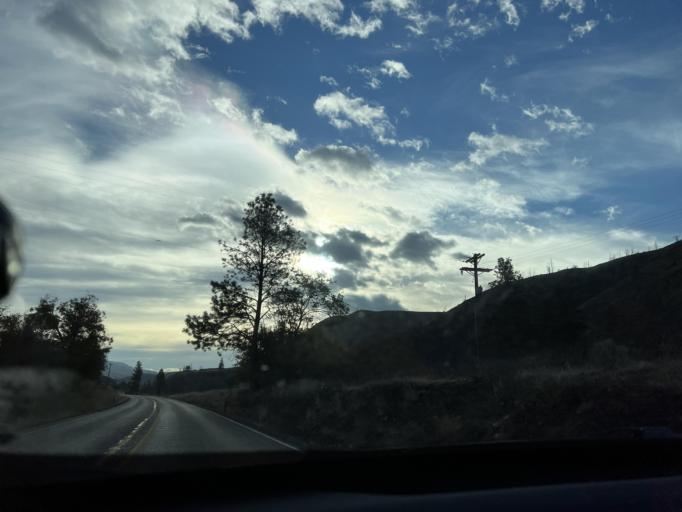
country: US
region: Washington
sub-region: Chelan County
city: Manson
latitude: 48.1554
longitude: -120.0662
